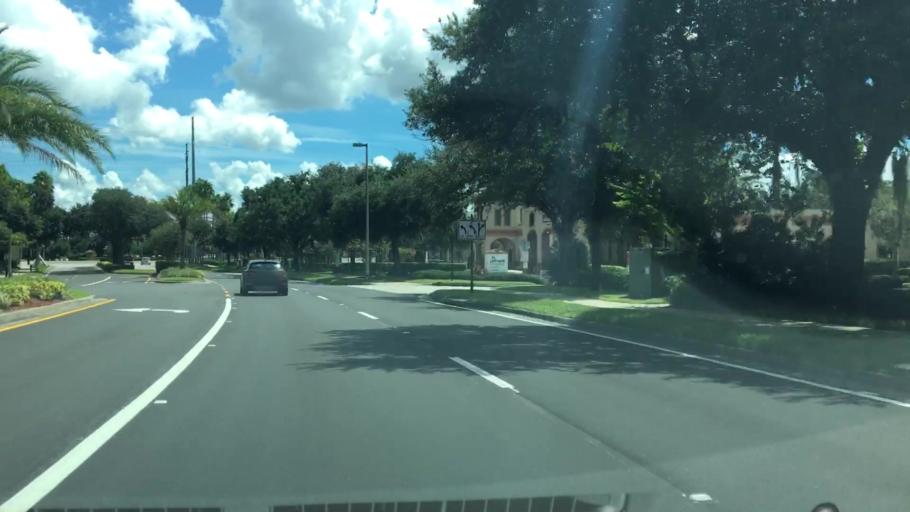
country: US
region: Florida
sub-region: Seminole County
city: Heathrow
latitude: 28.7653
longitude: -81.3494
